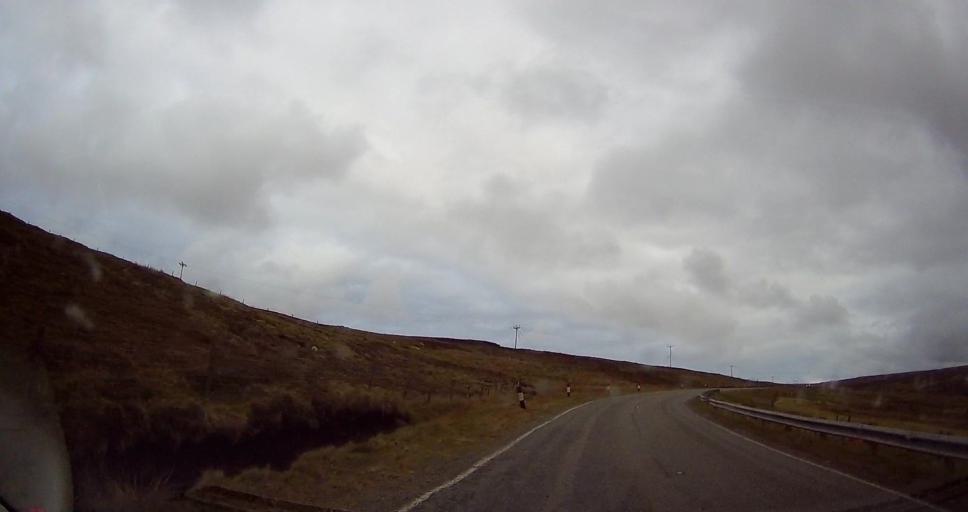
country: GB
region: Scotland
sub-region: Shetland Islands
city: Shetland
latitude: 60.6131
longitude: -1.0740
